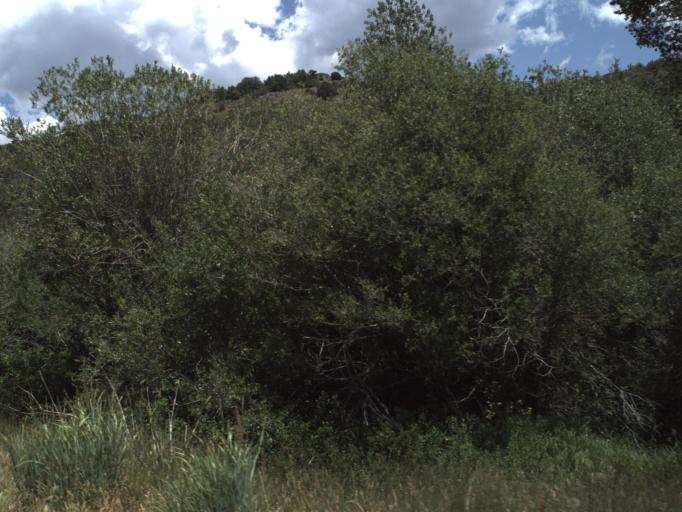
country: US
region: Utah
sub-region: Weber County
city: Wolf Creek
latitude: 41.3532
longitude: -111.5955
